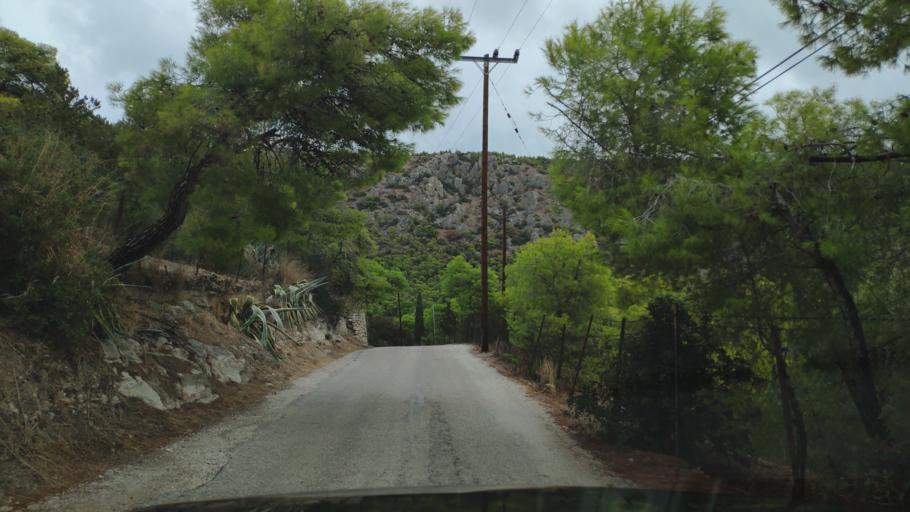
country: GR
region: Peloponnese
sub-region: Nomos Korinthias
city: Perachora
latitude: 38.0298
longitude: 22.8714
